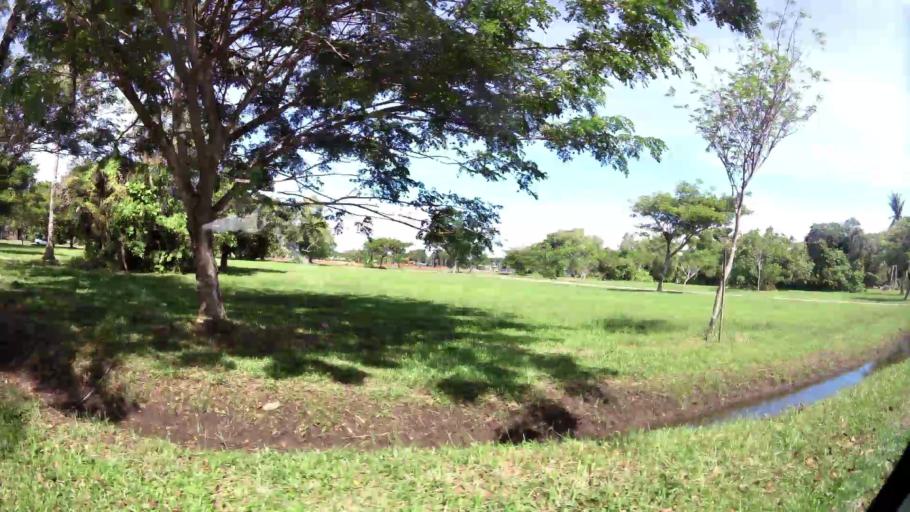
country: BN
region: Belait
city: Kuala Belait
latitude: 4.5878
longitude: 114.1986
